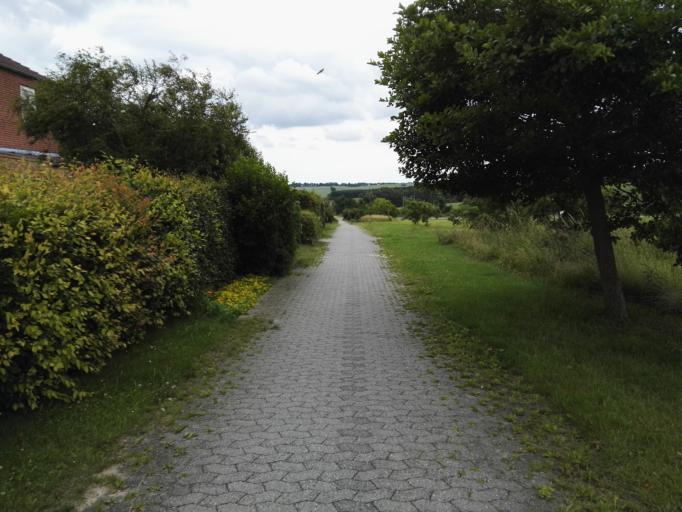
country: DK
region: Capital Region
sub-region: Egedal Kommune
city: Vekso
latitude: 55.7521
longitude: 12.2444
